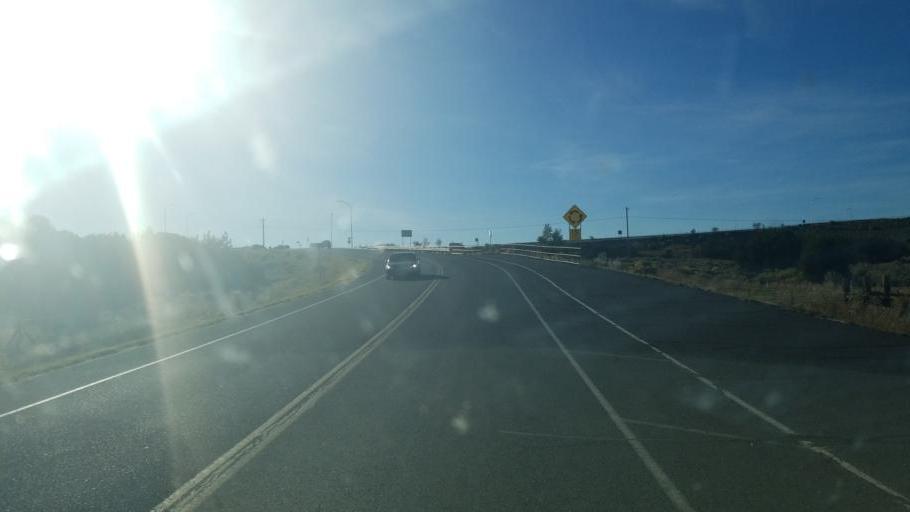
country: US
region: New Mexico
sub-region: Cibola County
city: Skyline-Ganipa
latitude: 35.0717
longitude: -107.5578
